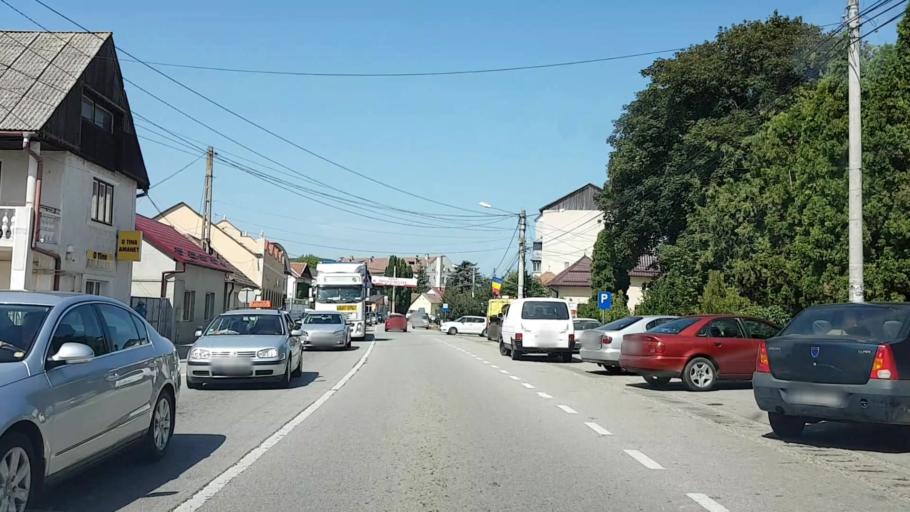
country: RO
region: Bistrita-Nasaud
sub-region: Comuna Beclean
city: Beclean
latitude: 47.1809
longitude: 24.1813
